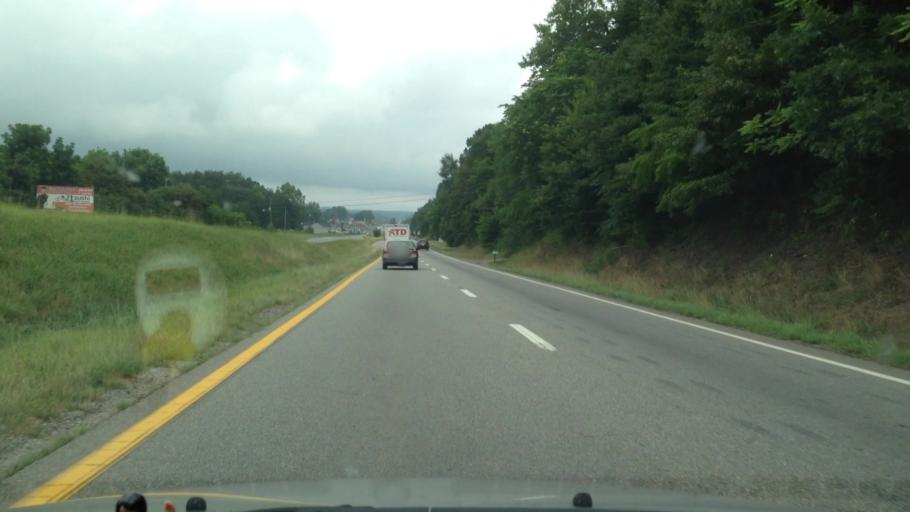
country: US
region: Virginia
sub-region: Henry County
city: Chatmoss
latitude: 36.5913
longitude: -79.8629
